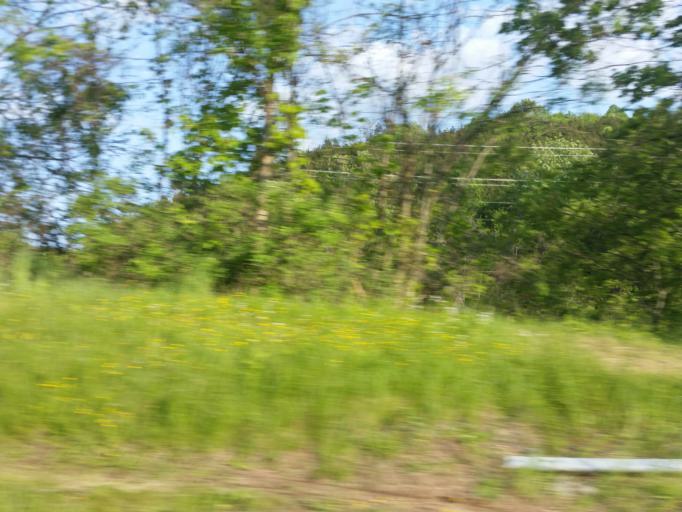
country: US
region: Virginia
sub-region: Tazewell County
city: Claypool Hill
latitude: 37.0512
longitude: -81.7748
